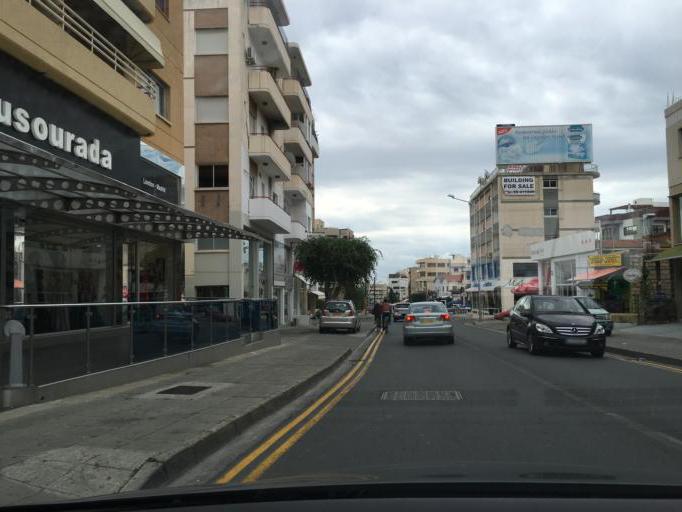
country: CY
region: Limassol
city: Limassol
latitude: 34.6866
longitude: 33.0442
